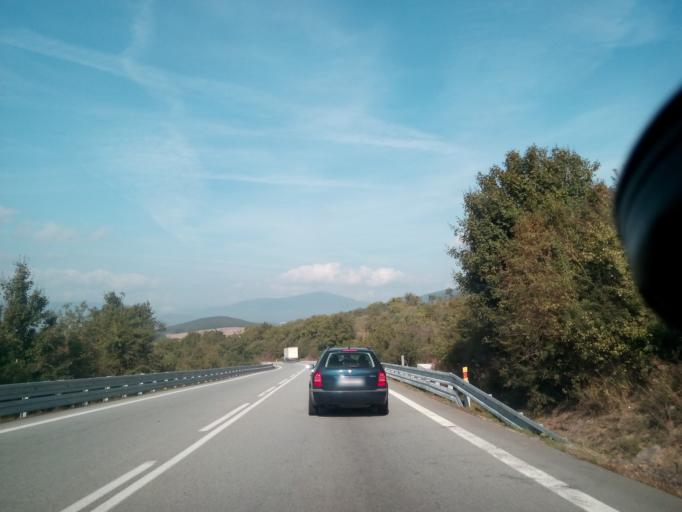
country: SK
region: Kosicky
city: Roznava
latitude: 48.6288
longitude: 20.6290
